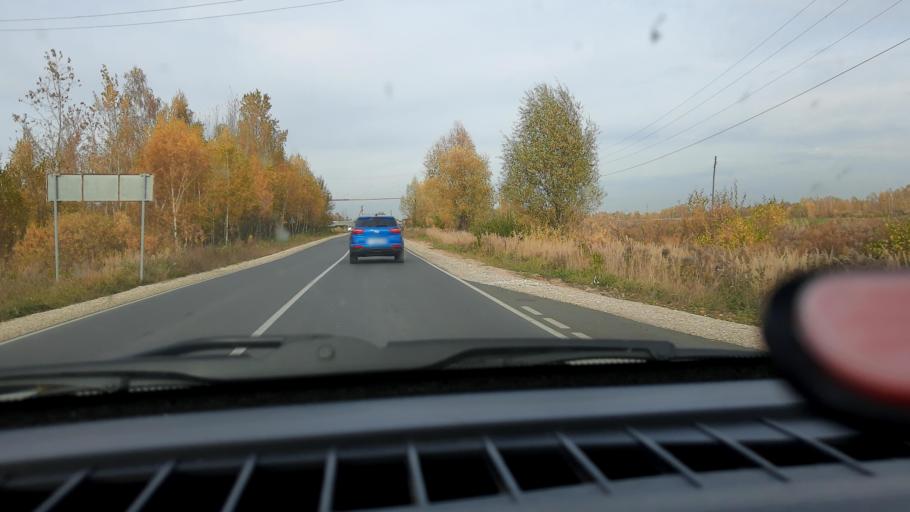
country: RU
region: Nizjnij Novgorod
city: Neklyudovo
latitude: 56.4481
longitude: 43.8998
